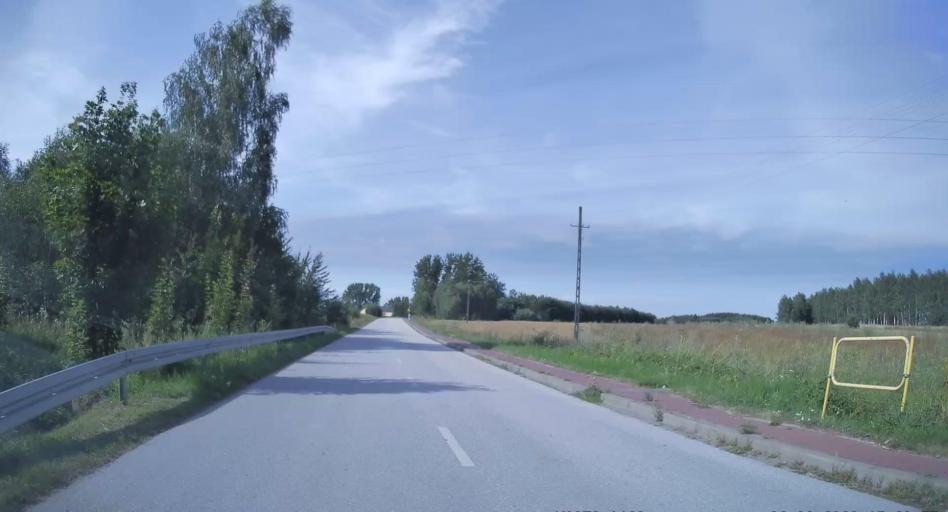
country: PL
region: Lodz Voivodeship
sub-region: Powiat opoczynski
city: Mniszkow
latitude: 51.3456
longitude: 20.0386
